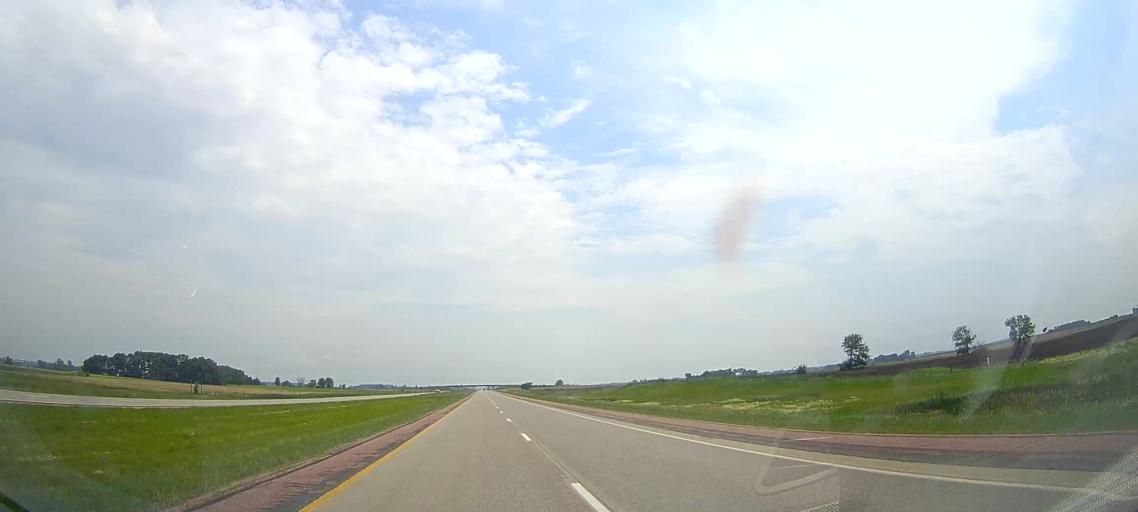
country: US
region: South Dakota
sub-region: Union County
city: Beresford
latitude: 42.9616
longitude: -96.7950
